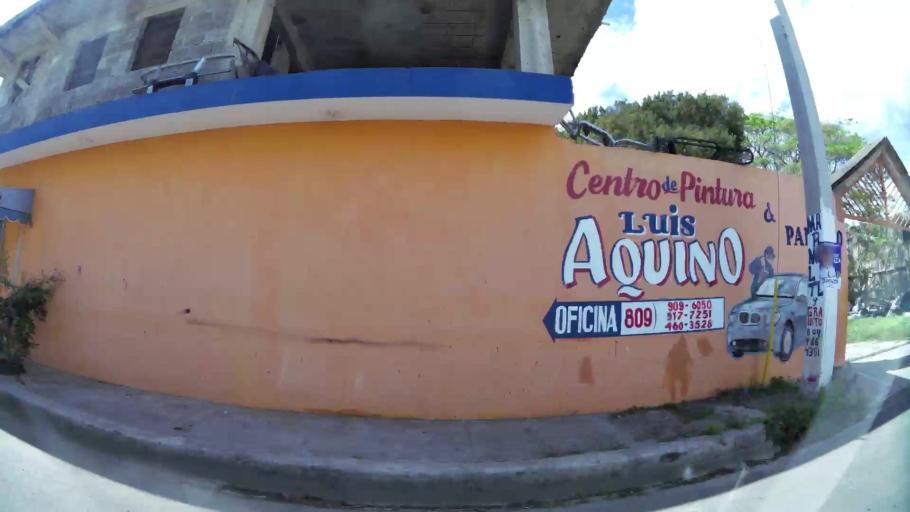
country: DO
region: Santiago
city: Santiago de los Caballeros
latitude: 19.4713
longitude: -70.7011
